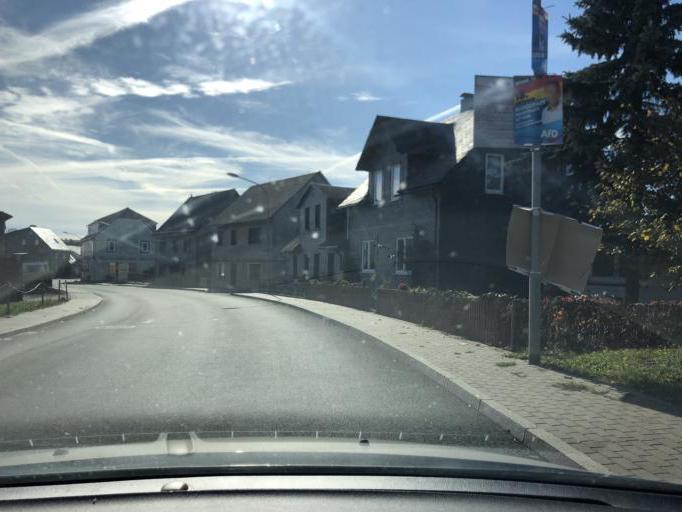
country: DE
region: Thuringia
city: Reichmannsdorf
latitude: 50.5495
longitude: 11.2599
